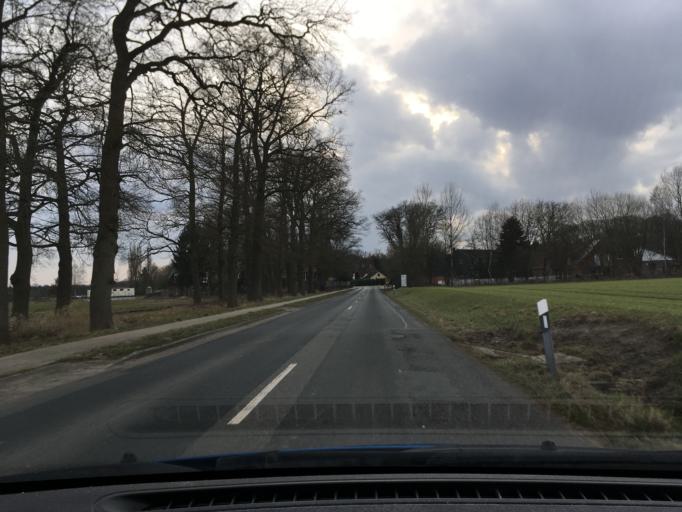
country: DE
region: Lower Saxony
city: Reppenstedt
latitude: 53.2552
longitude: 10.3223
